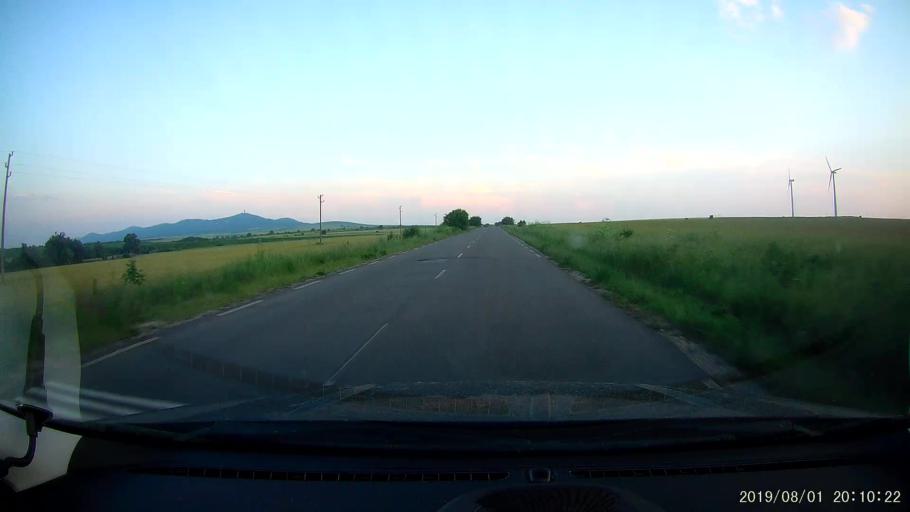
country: BG
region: Yambol
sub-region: Obshtina Yambol
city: Yambol
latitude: 42.4828
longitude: 26.5986
